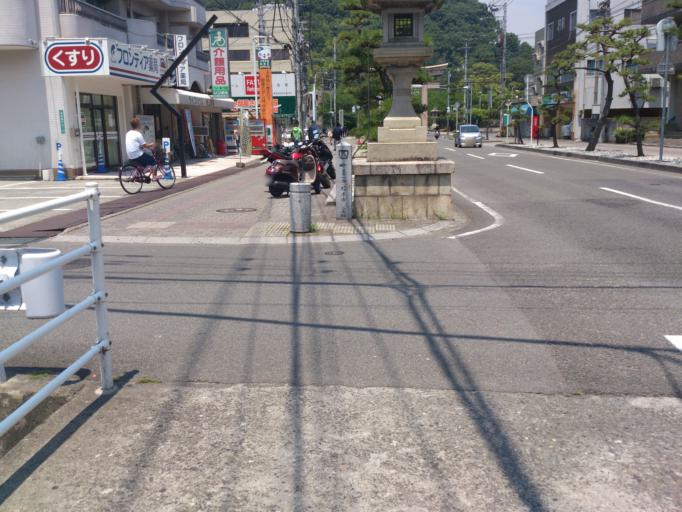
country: JP
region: Ehime
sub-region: Shikoku-chuo Shi
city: Matsuyama
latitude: 33.8514
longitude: 132.7736
